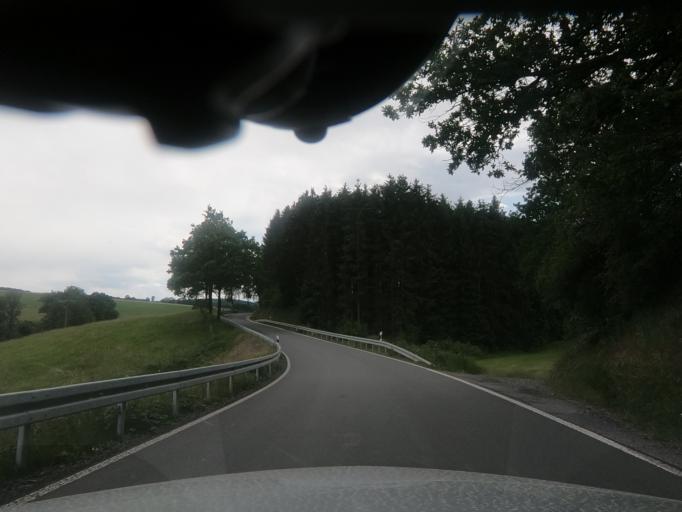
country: DE
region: North Rhine-Westphalia
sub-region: Regierungsbezirk Arnsberg
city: Arnsberg
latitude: 51.3264
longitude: 8.1207
